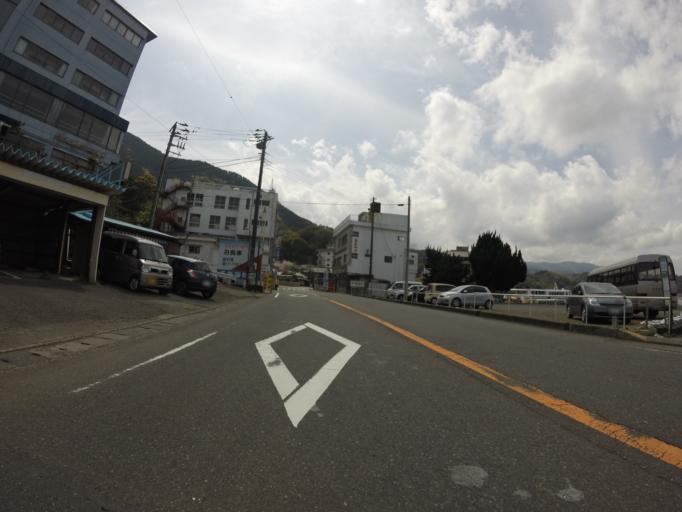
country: JP
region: Shizuoka
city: Numazu
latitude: 35.0216
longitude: 138.8977
